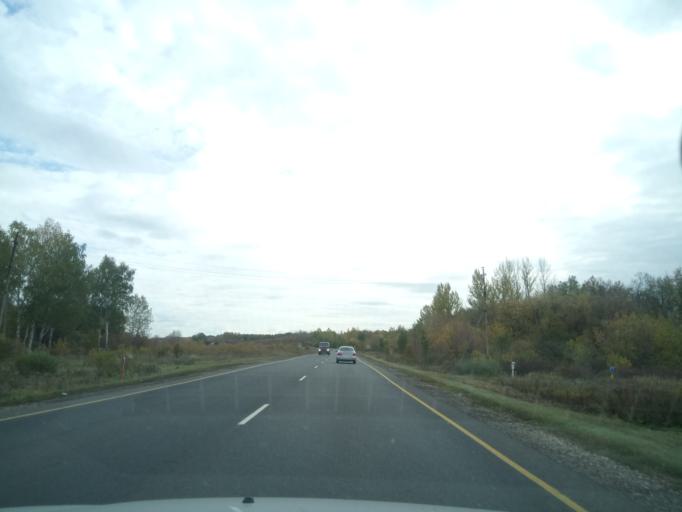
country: RU
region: Nizjnij Novgorod
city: Lukoyanov
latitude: 55.0536
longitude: 44.3722
